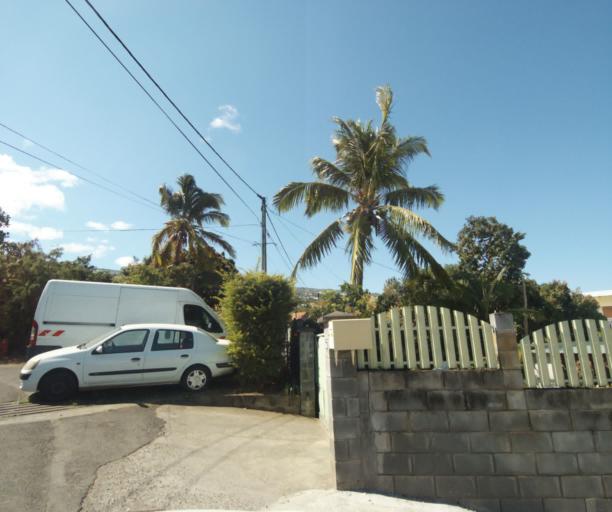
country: RE
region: Reunion
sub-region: Reunion
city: La Possession
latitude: -20.9825
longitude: 55.3250
